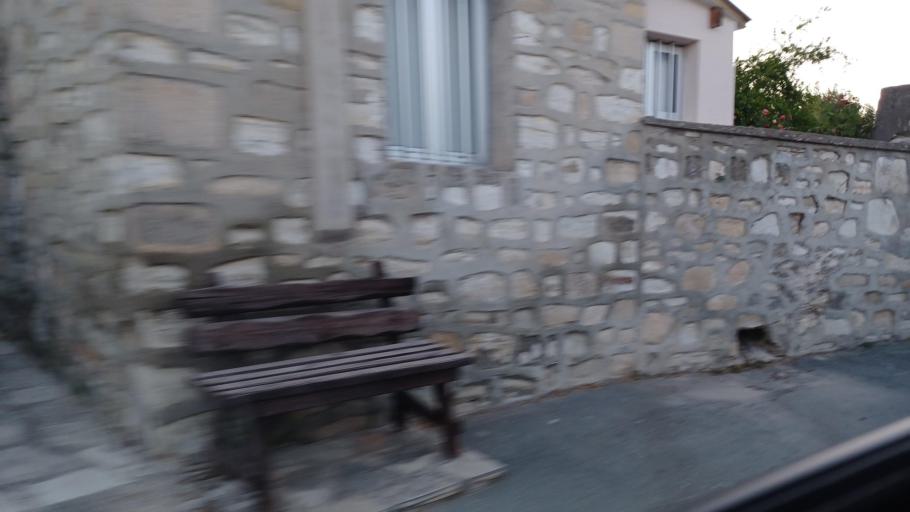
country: CY
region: Pafos
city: Mesogi
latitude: 34.8248
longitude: 32.5811
